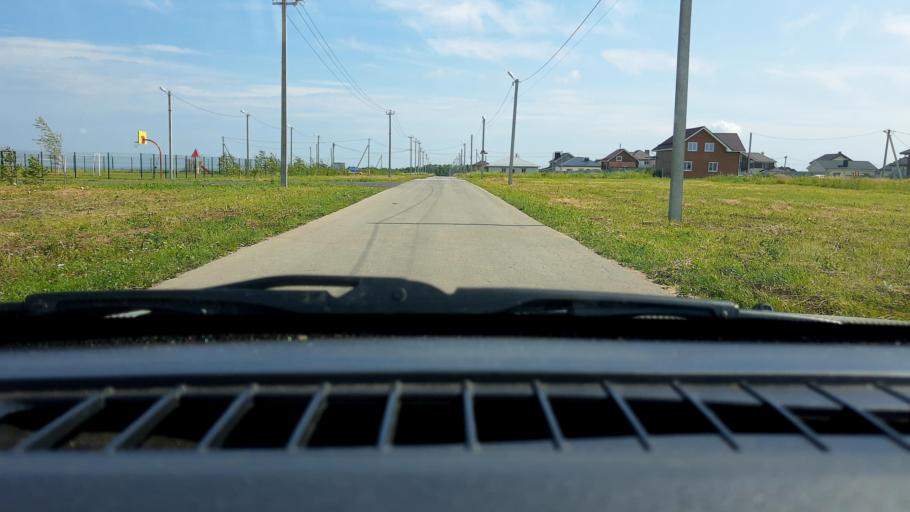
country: RU
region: Nizjnij Novgorod
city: Burevestnik
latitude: 56.1476
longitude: 43.7249
